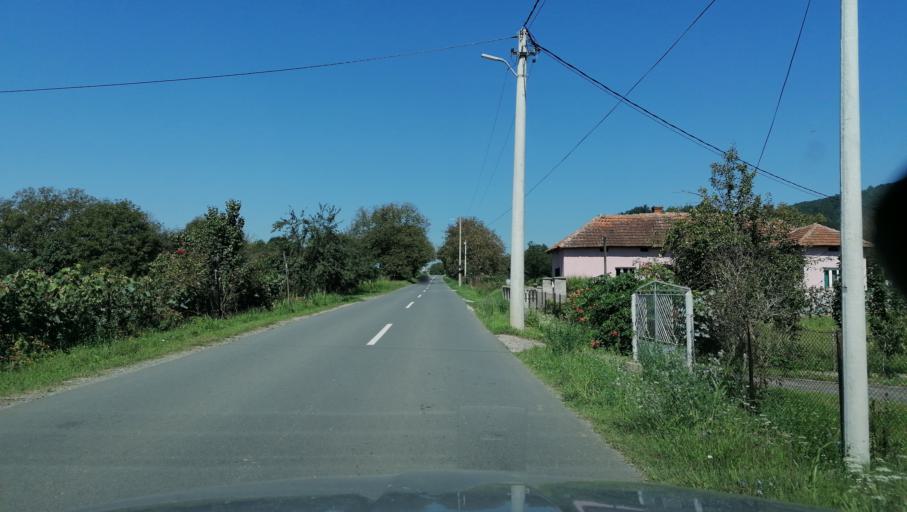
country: RS
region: Central Serbia
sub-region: Raski Okrug
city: Vrnjacka Banja
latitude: 43.6728
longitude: 20.9037
